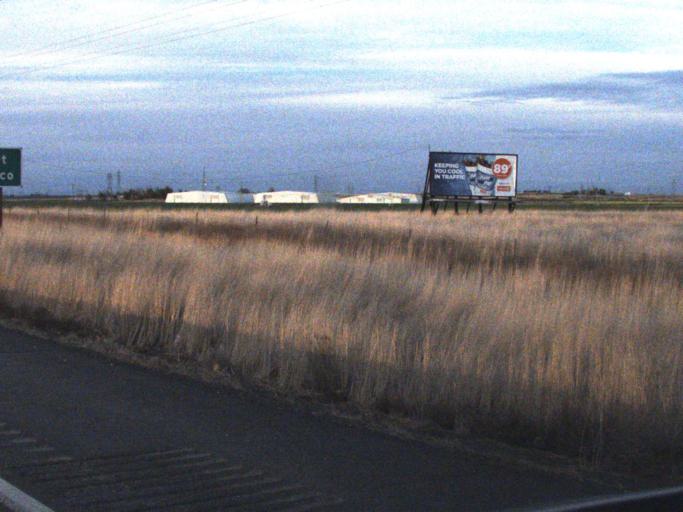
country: US
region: Washington
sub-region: Walla Walla County
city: Burbank
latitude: 46.2250
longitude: -119.0357
